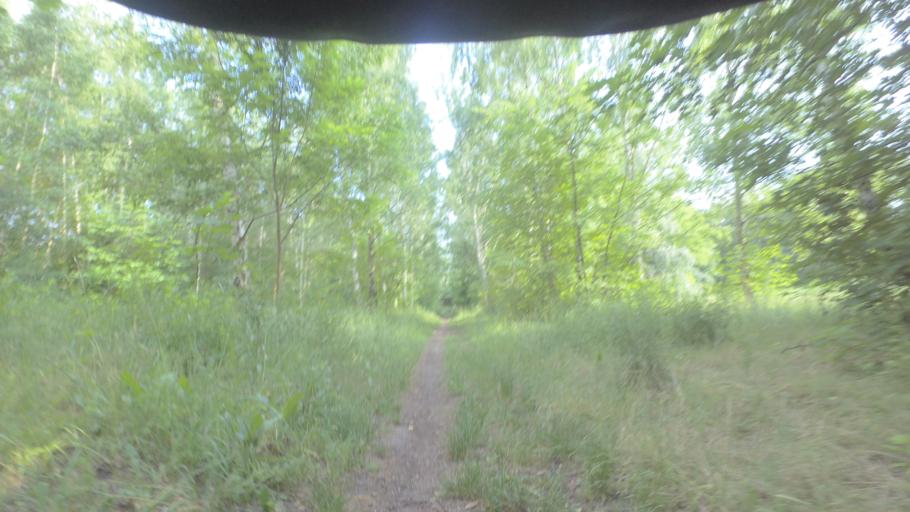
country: DE
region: Berlin
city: Lichtenrade
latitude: 52.3991
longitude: 13.4227
